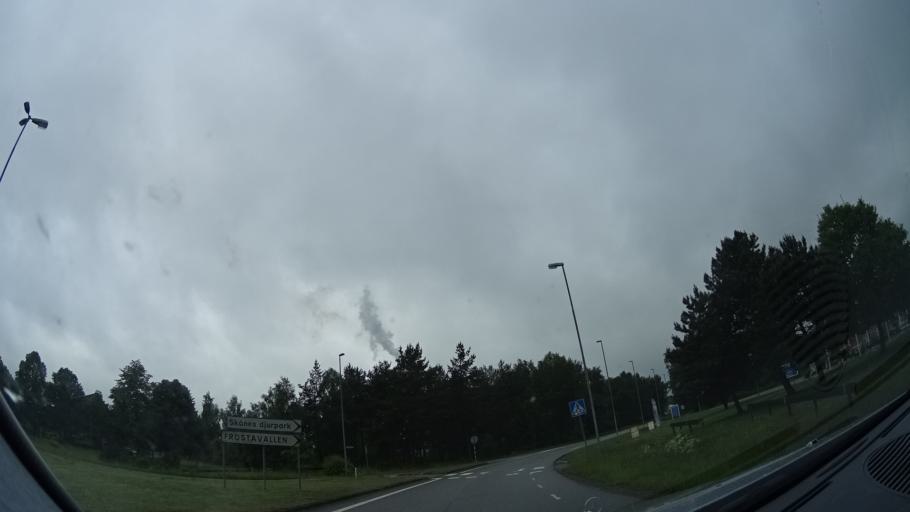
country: SE
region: Skane
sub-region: Hoors Kommun
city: Hoeoer
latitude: 55.9364
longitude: 13.5549
